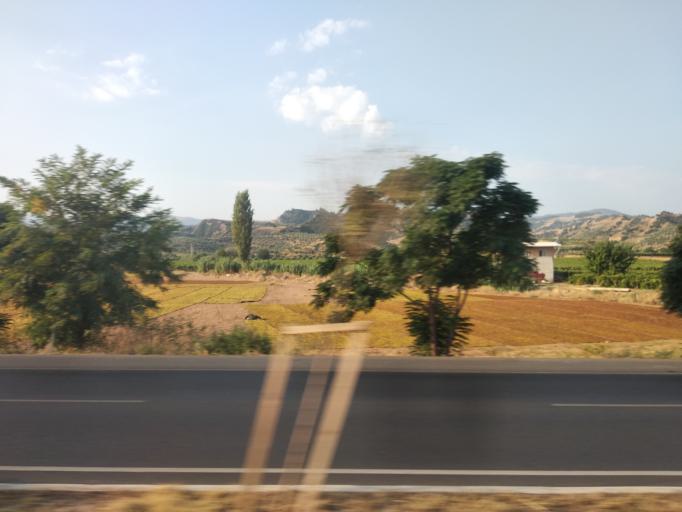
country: TR
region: Manisa
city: Ahmetli
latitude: 38.5067
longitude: 27.9941
